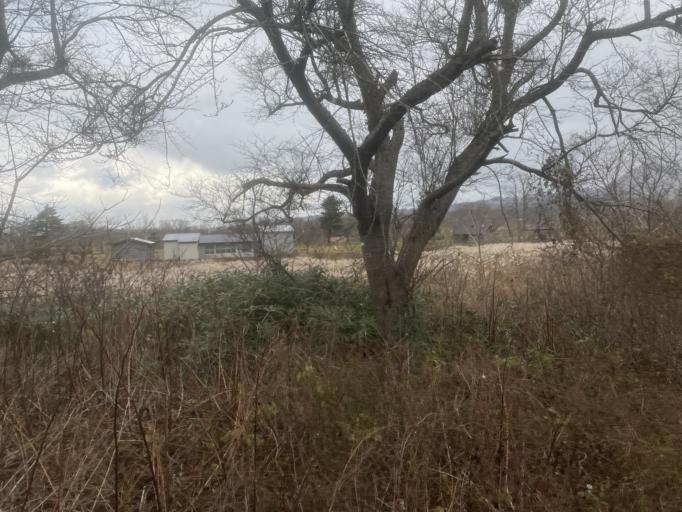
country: JP
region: Aomori
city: Goshogawara
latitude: 41.1798
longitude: 140.4906
